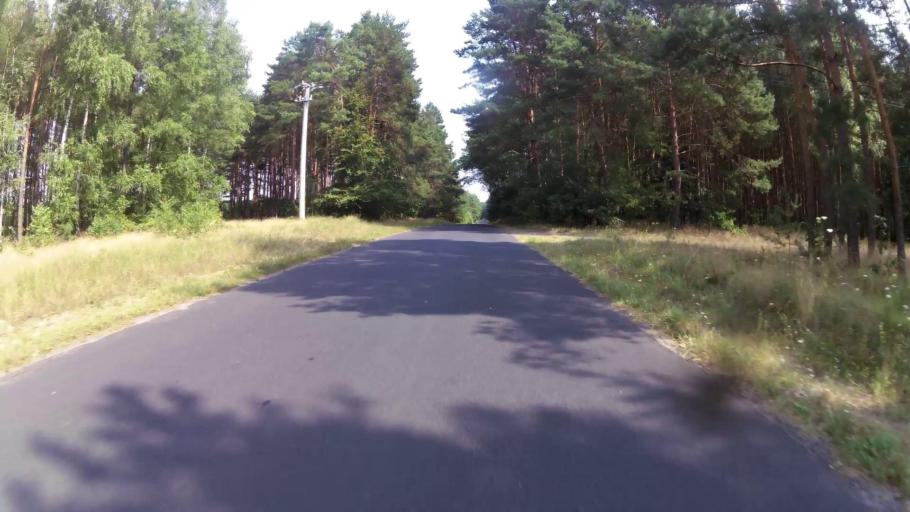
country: PL
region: West Pomeranian Voivodeship
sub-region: Powiat mysliborski
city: Debno
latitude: 52.8453
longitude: 14.7609
